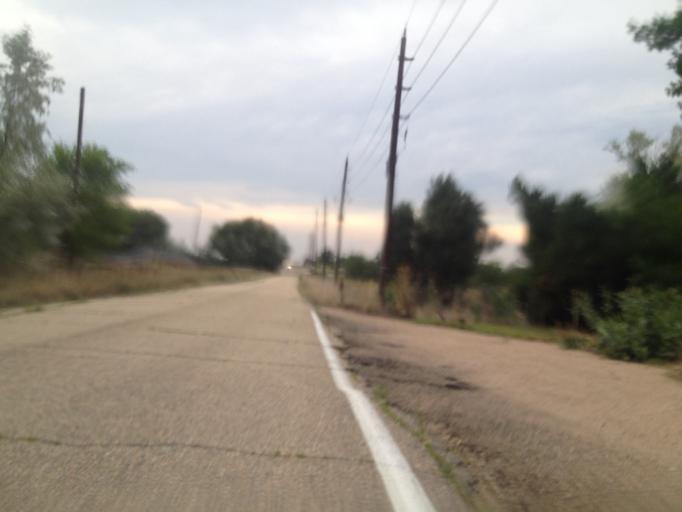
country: US
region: Colorado
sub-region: Boulder County
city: Louisville
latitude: 39.9481
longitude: -105.1281
